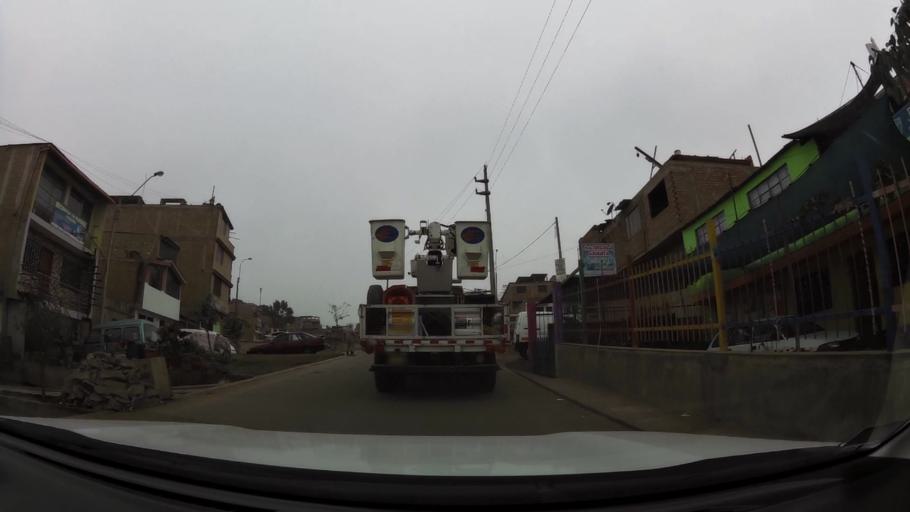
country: PE
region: Lima
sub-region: Lima
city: Surco
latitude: -12.1709
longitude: -76.9577
